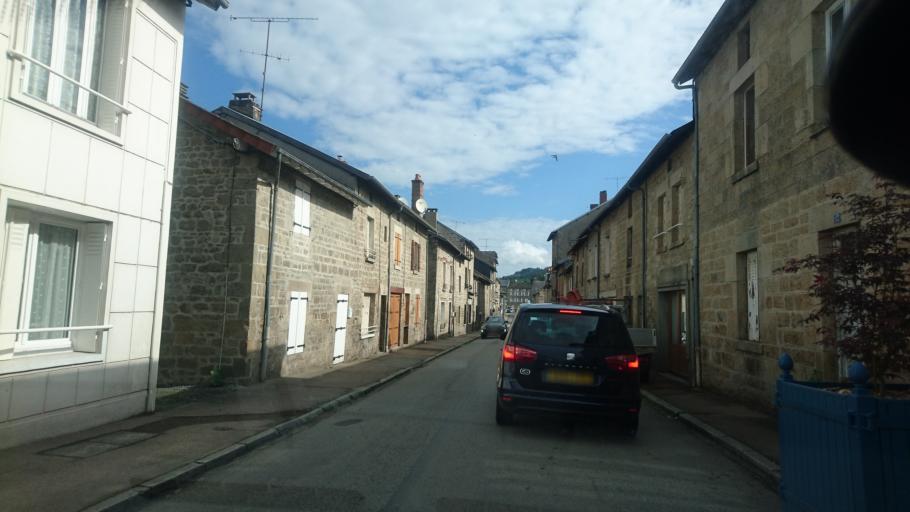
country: FR
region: Limousin
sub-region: Departement de la Haute-Vienne
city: Peyrat-le-Chateau
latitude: 45.8128
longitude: 1.7720
